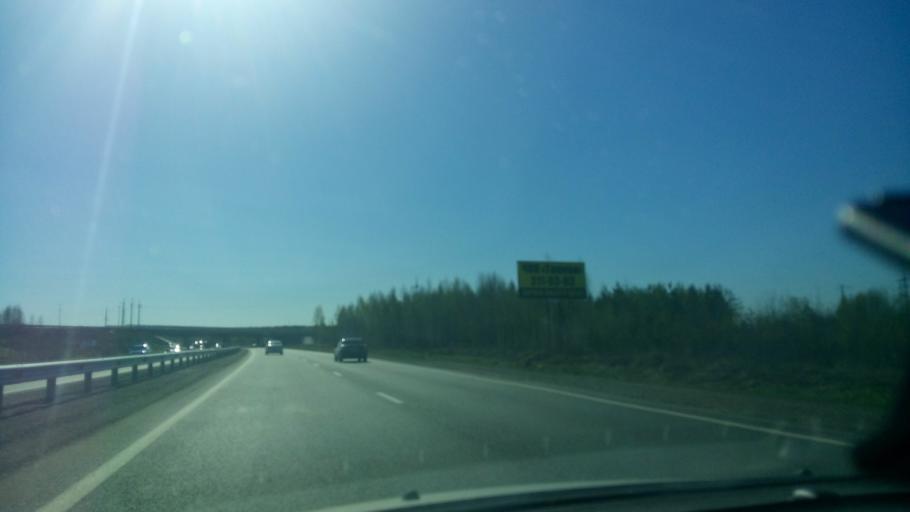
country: RU
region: Sverdlovsk
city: Verkhneye Dubrovo
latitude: 56.7360
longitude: 61.0184
